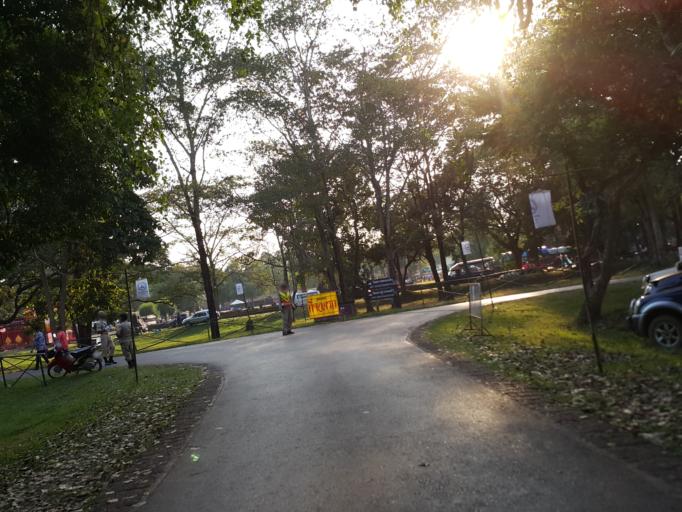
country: TH
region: Sukhothai
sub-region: Amphoe Si Satchanalai
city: Si Satchanalai
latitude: 17.4327
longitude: 99.7866
